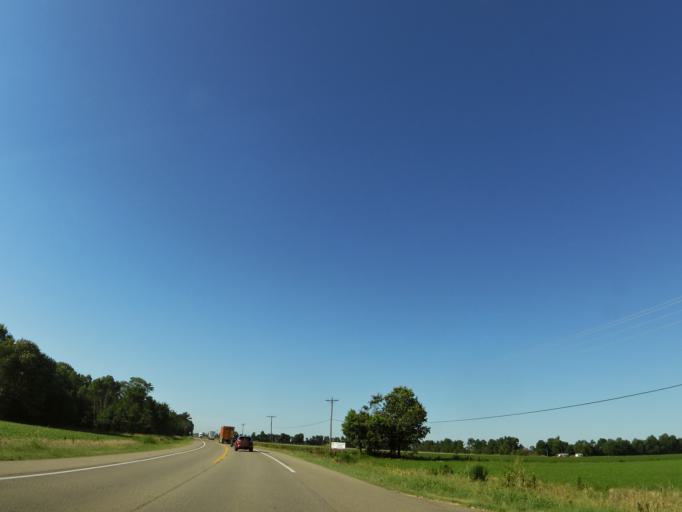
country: US
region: Arkansas
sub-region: Clay County
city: Corning
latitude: 36.4523
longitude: -90.5853
